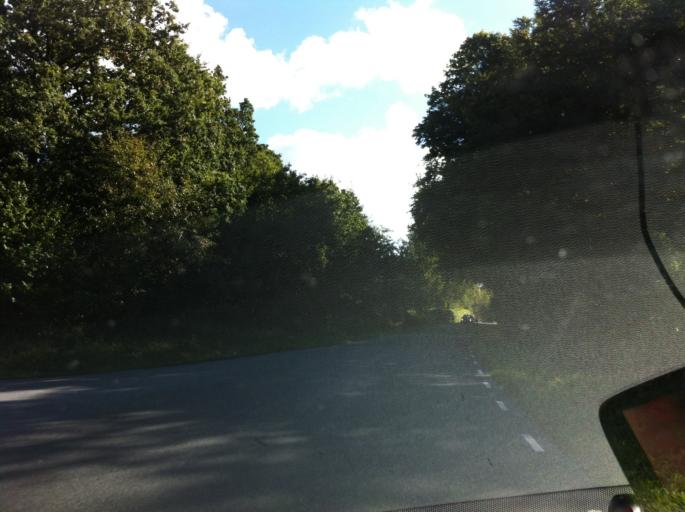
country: SE
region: Skane
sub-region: Kristianstads Kommun
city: Degeberga
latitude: 55.7461
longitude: 13.9420
